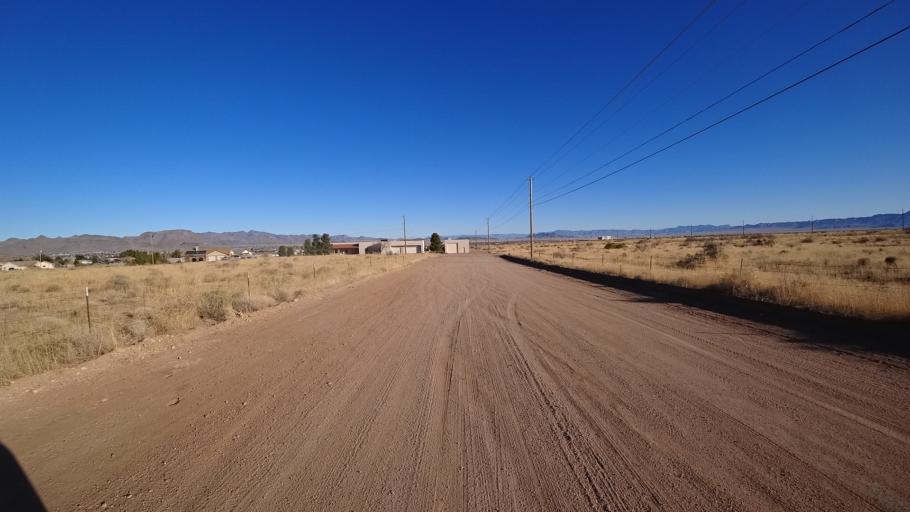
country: US
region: Arizona
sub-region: Mohave County
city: Kingman
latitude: 35.2022
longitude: -113.9939
